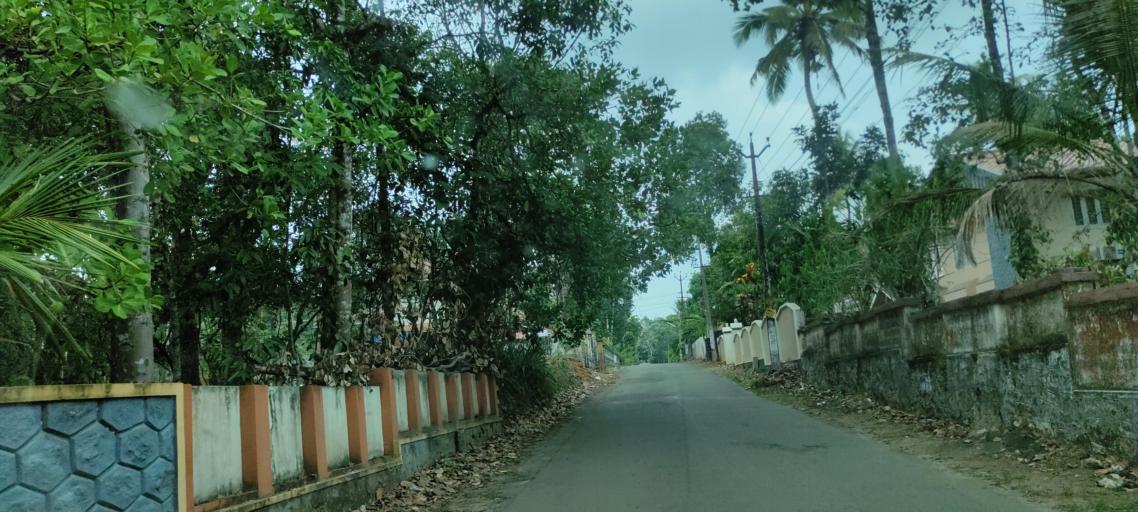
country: IN
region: Kerala
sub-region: Pattanamtitta
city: Adur
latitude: 9.1719
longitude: 76.7372
